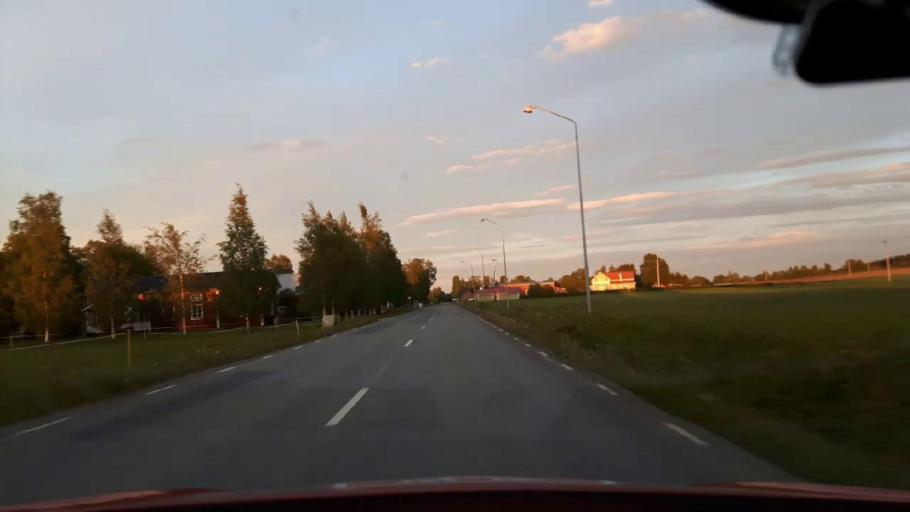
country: SE
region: Jaemtland
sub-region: OEstersunds Kommun
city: Ostersund
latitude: 63.1189
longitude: 14.7180
